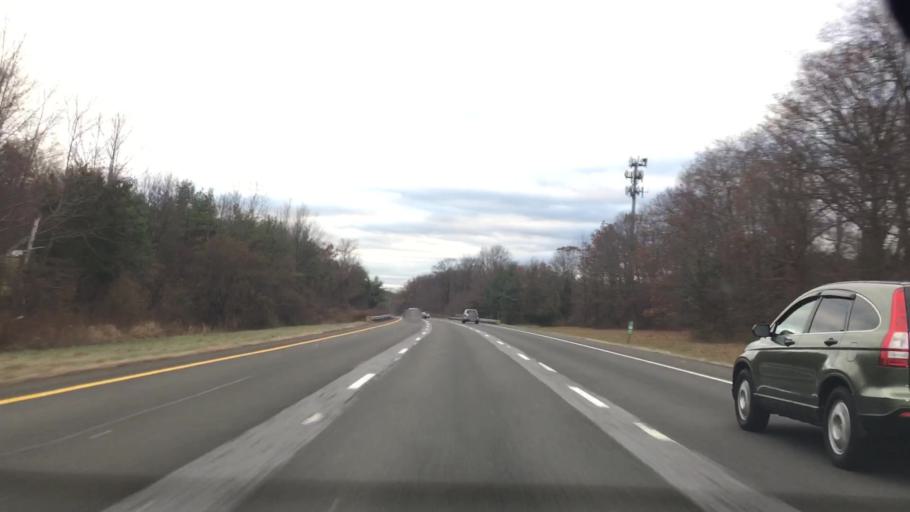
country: US
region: New York
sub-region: Westchester County
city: Armonk
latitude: 41.1643
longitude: -73.6889
